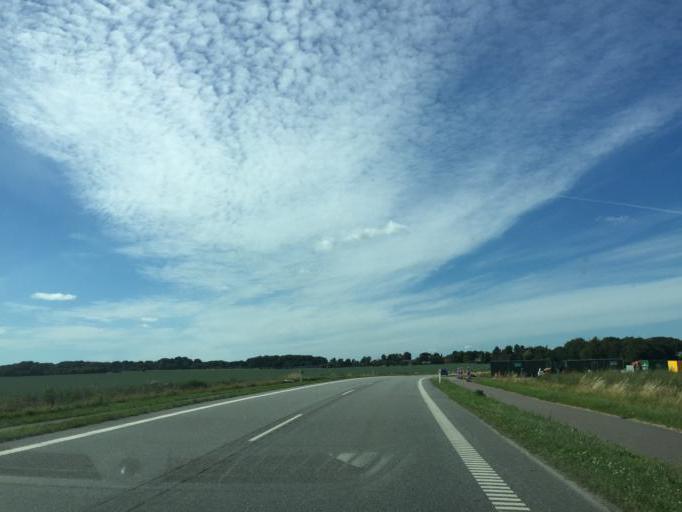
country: DK
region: South Denmark
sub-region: Odense Kommune
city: Hojby
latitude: 55.3398
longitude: 10.3825
